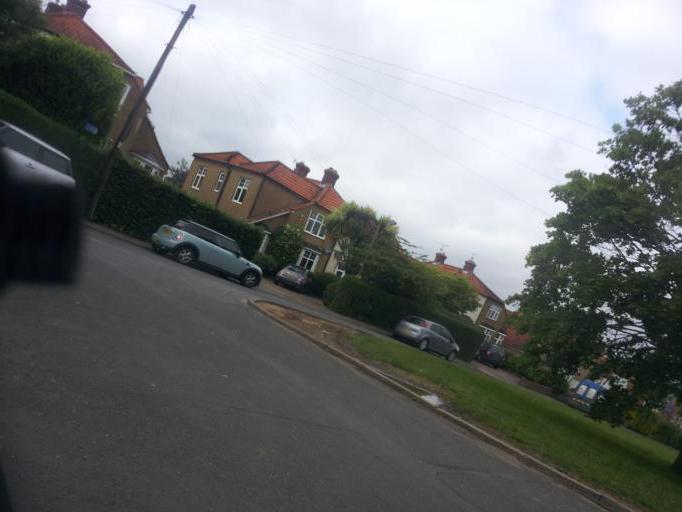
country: GB
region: England
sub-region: Kent
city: Maidstone
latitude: 51.2830
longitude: 0.5017
